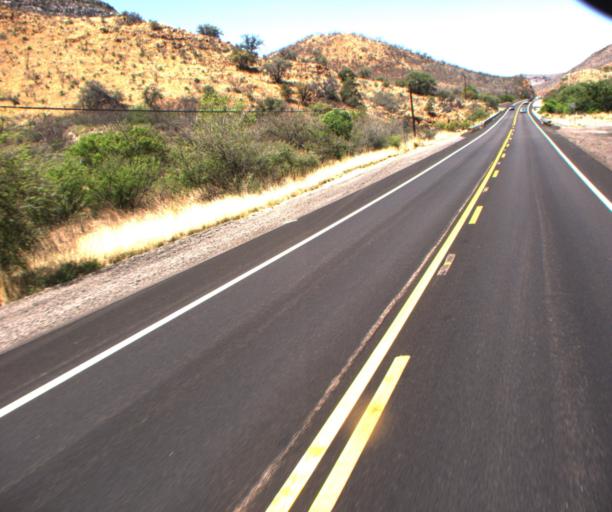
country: US
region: Arizona
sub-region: Cochise County
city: Bisbee
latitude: 31.5010
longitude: -110.0042
